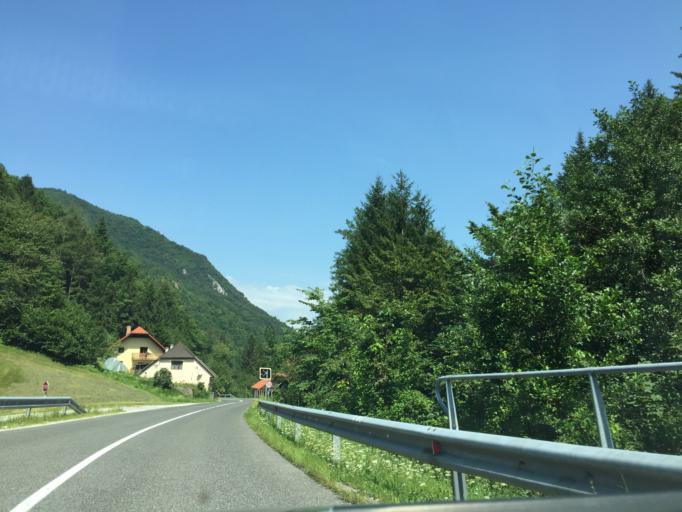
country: SI
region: Prebold
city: Prebold
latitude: 46.2003
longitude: 15.0732
